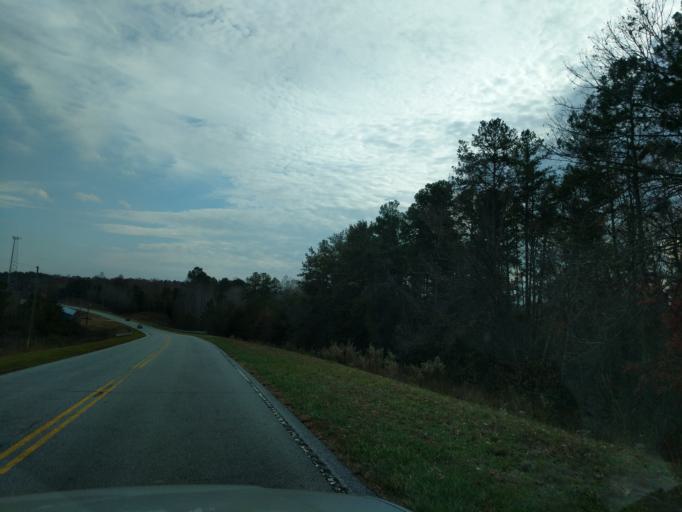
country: US
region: Georgia
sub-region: Franklin County
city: Gumlog
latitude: 34.5023
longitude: -83.0396
